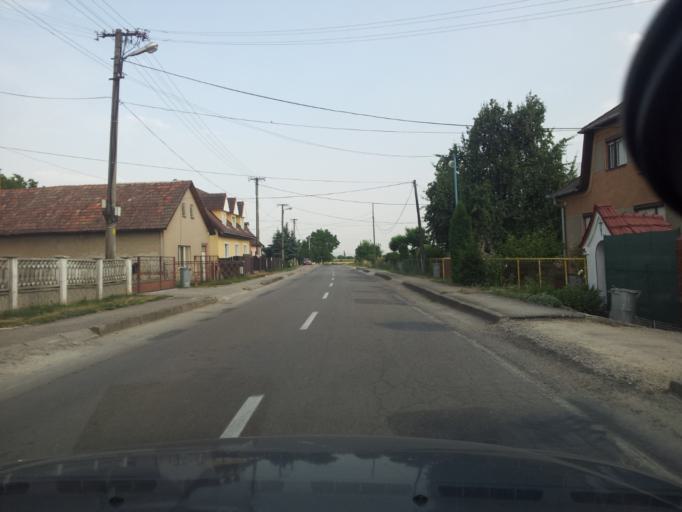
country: SK
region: Nitriansky
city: Banovce nad Bebravou
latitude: 48.7768
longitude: 18.1995
